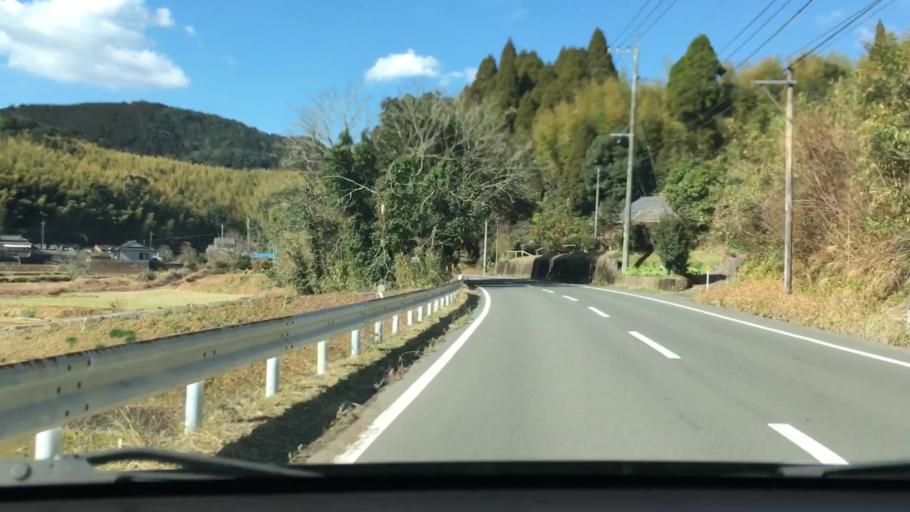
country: JP
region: Kagoshima
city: Ijuin
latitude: 31.7064
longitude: 130.4448
